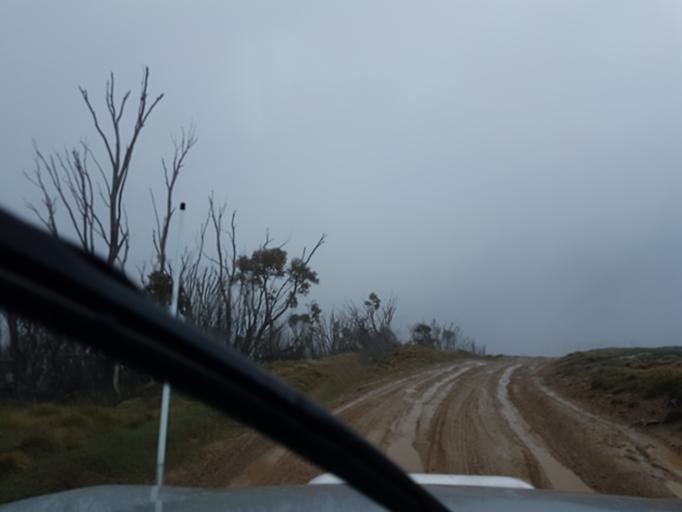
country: AU
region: Victoria
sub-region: Alpine
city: Mount Beauty
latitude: -37.0855
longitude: 147.1164
